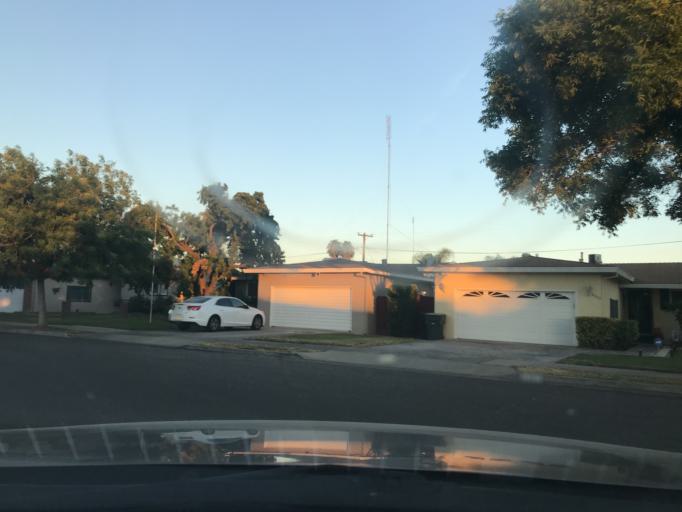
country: US
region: California
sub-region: Merced County
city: Atwater
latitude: 37.3559
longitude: -120.5971
